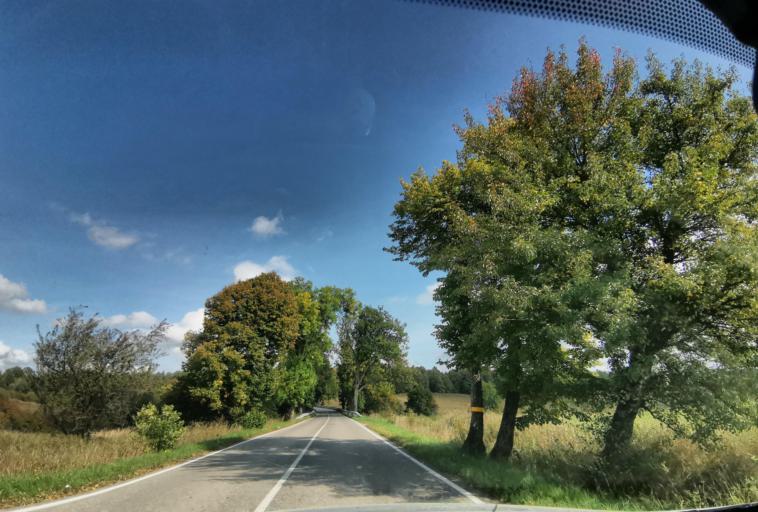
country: PL
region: Warmian-Masurian Voivodeship
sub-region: Powiat goldapski
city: Goldap
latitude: 54.4581
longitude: 22.3766
